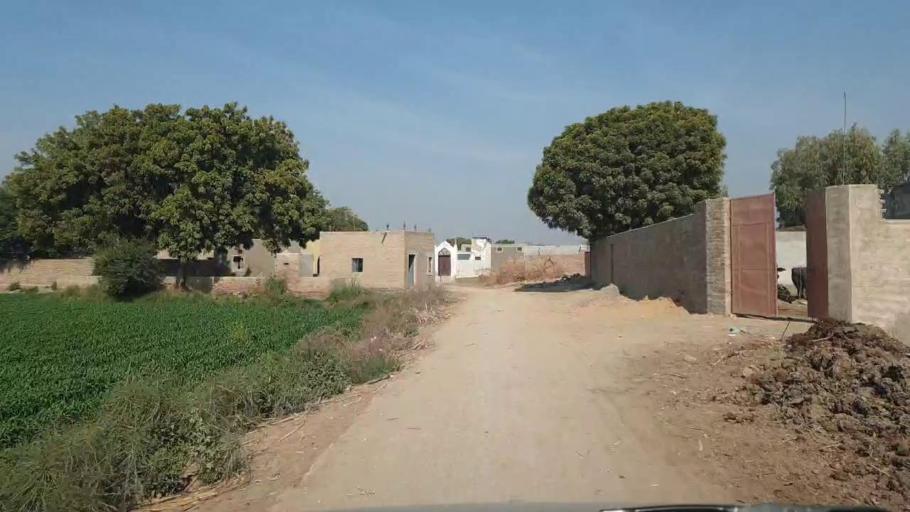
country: PK
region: Sindh
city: Tando Allahyar
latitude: 25.4036
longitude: 68.7439
